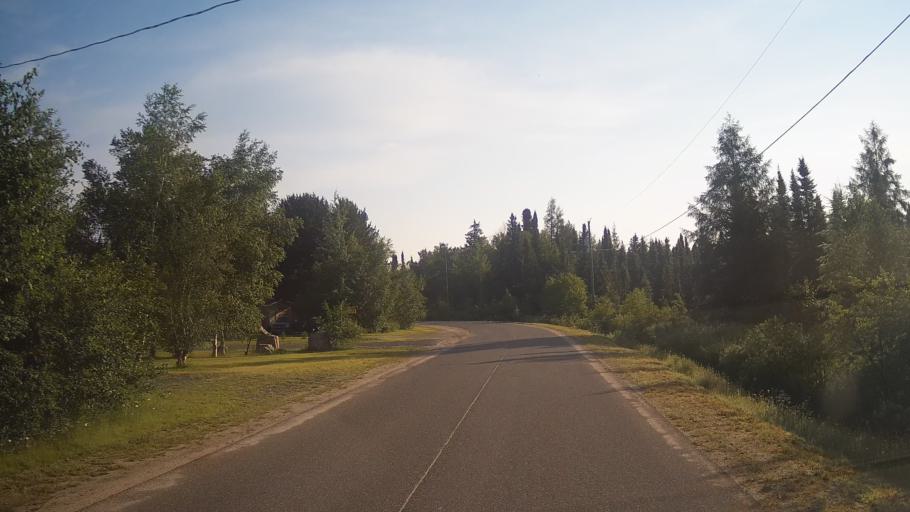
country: CA
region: Ontario
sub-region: Rainy River District
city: Atikokan
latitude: 49.3993
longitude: -91.6665
